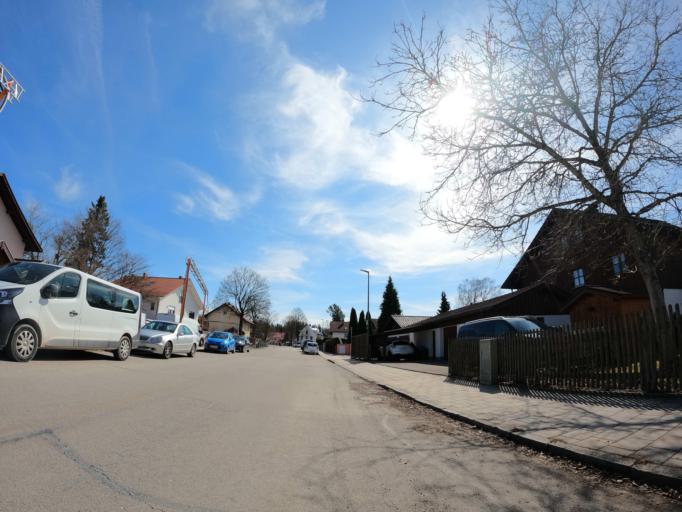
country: DE
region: Bavaria
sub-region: Upper Bavaria
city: Hohenkirchen-Siegertsbrunn
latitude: 48.0157
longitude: 11.7131
